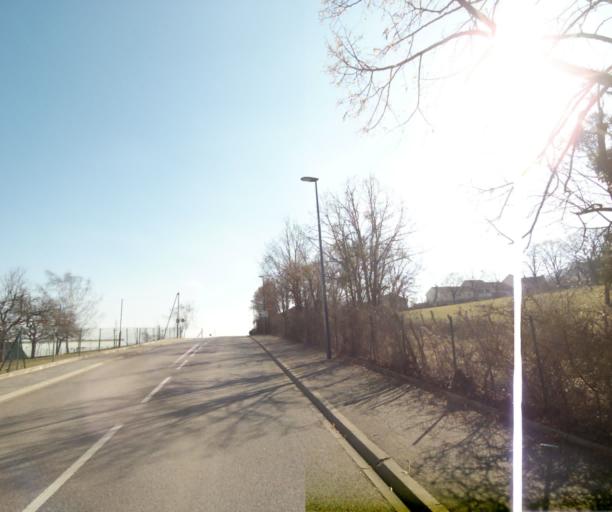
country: FR
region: Lorraine
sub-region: Departement de Meurthe-et-Moselle
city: Vandoeuvre-les-Nancy
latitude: 48.6439
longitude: 6.1766
